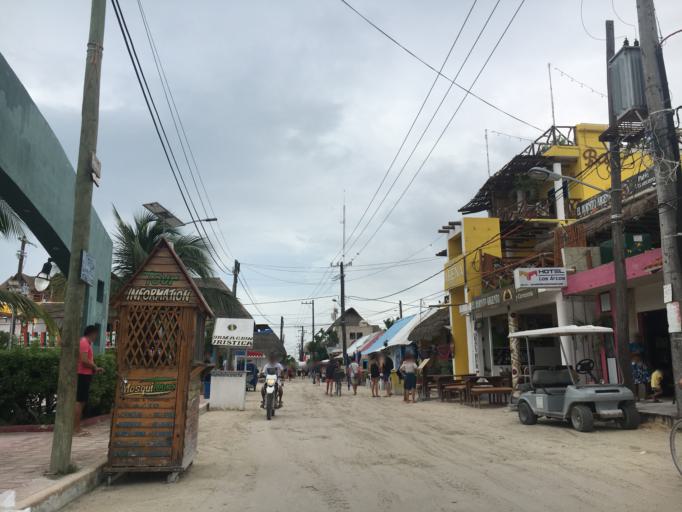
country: MX
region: Quintana Roo
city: Kantunilkin
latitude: 21.5235
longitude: -87.3792
